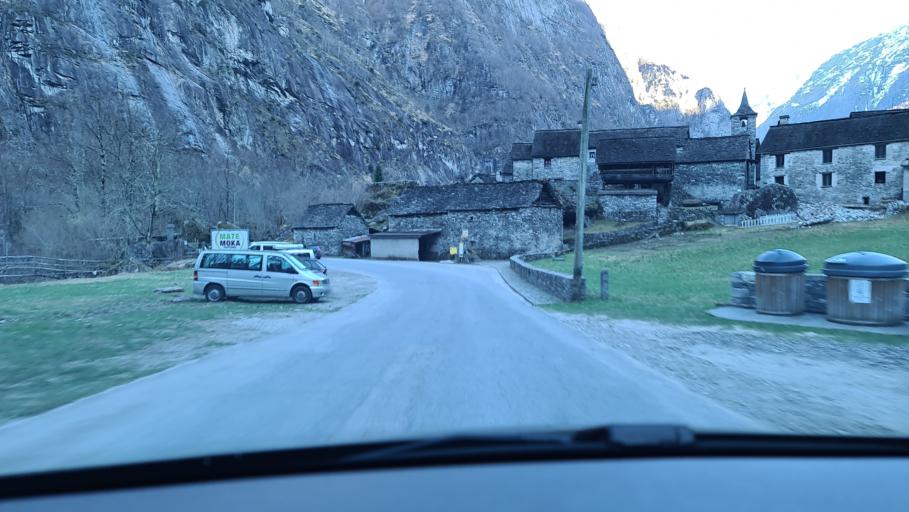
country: CH
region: Ticino
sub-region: Vallemaggia District
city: Cevio
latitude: 46.3951
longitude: 8.5369
